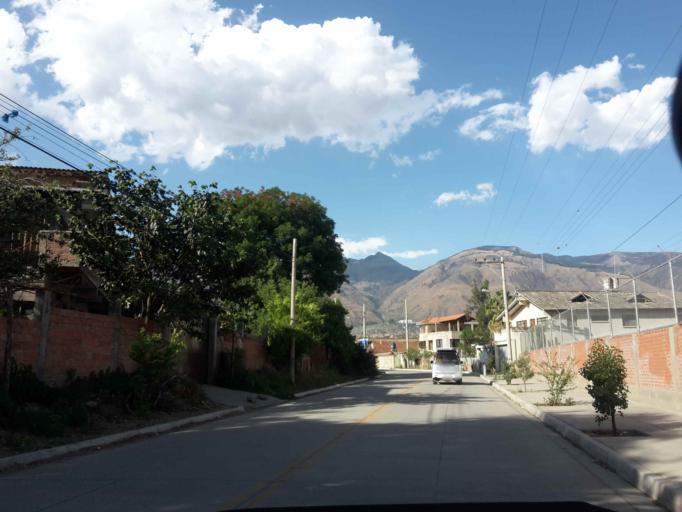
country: BO
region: Cochabamba
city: Cochabamba
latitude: -17.3619
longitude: -66.2075
